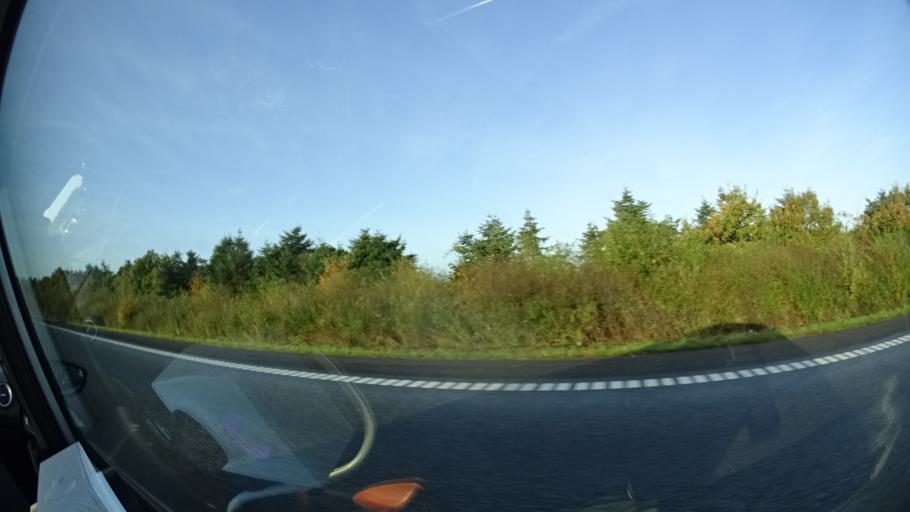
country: DK
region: Central Jutland
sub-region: Skanderborg Kommune
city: Skanderborg
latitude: 55.9998
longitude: 9.8702
